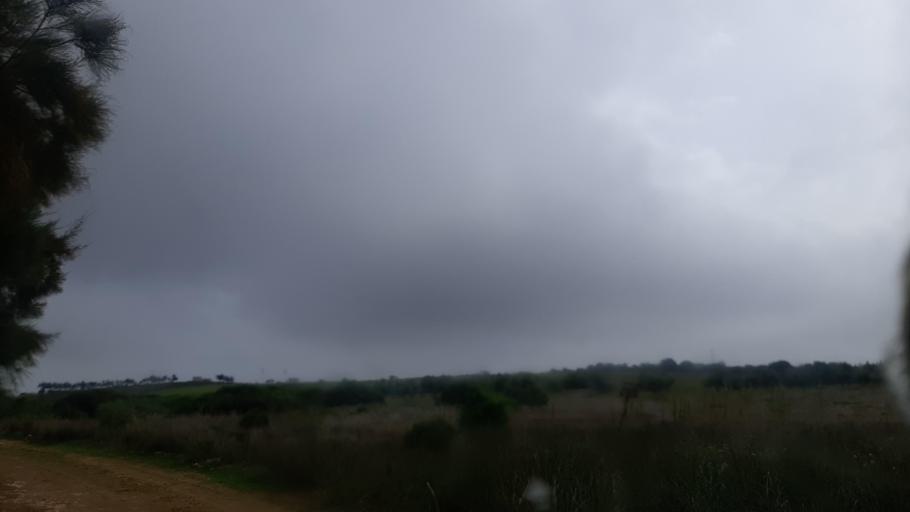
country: TN
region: Nabul
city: Qulaybiyah
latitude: 36.8252
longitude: 11.0367
